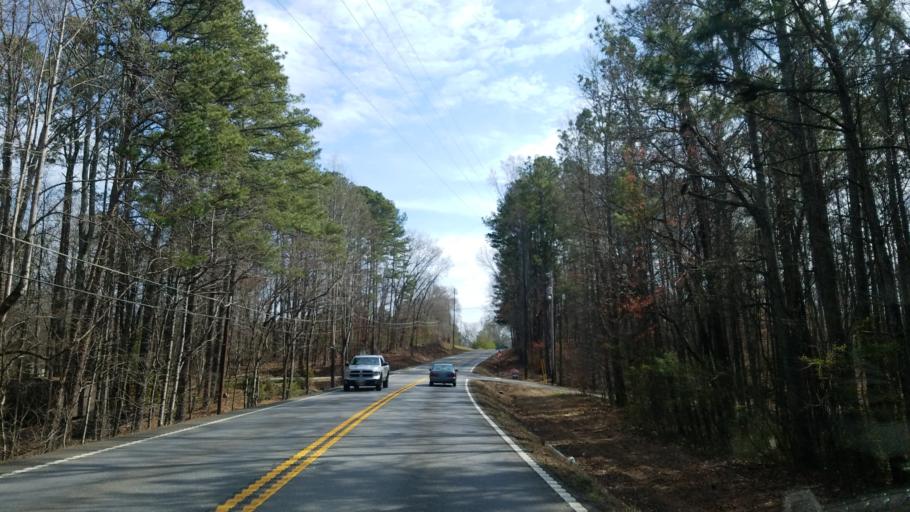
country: US
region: Georgia
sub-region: Cherokee County
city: Canton
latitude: 34.2146
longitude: -84.4575
